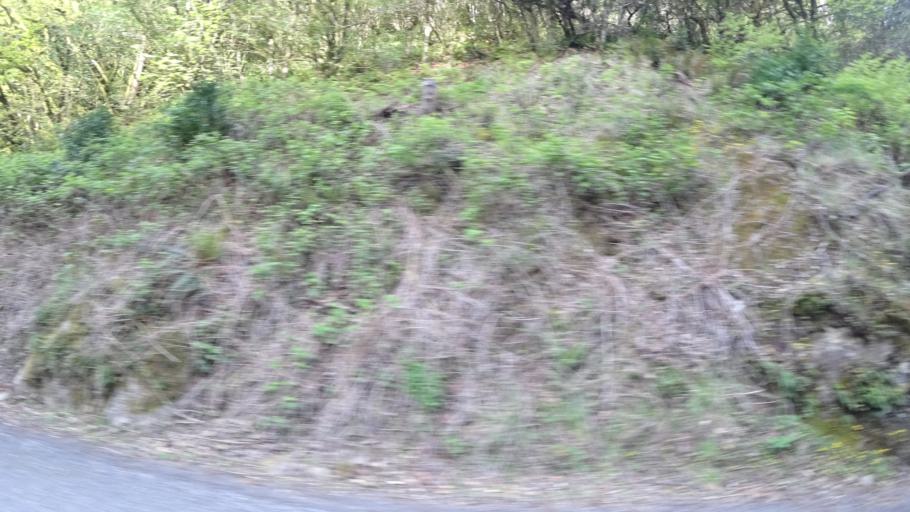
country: US
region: Oregon
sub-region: Curry County
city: Port Orford
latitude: 42.6854
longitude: -124.4267
